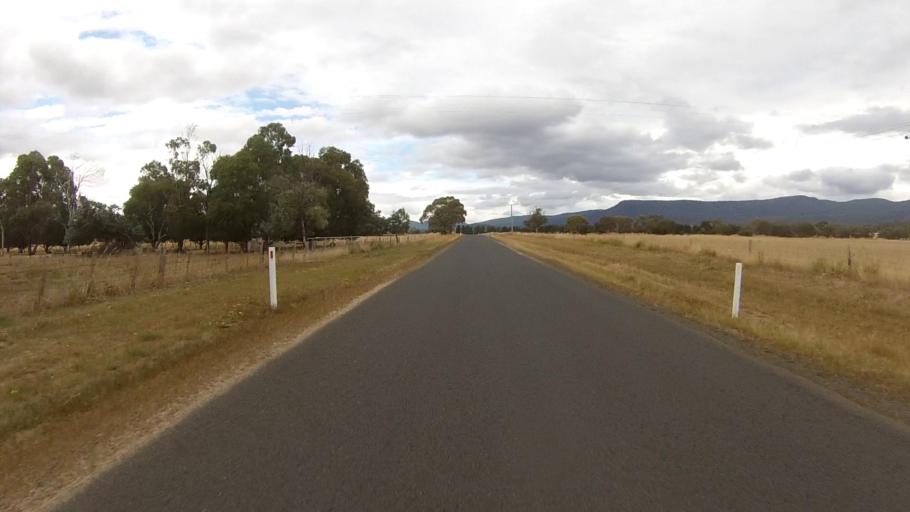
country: AU
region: Tasmania
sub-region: Northern Midlands
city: Evandale
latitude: -41.8241
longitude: 147.8306
